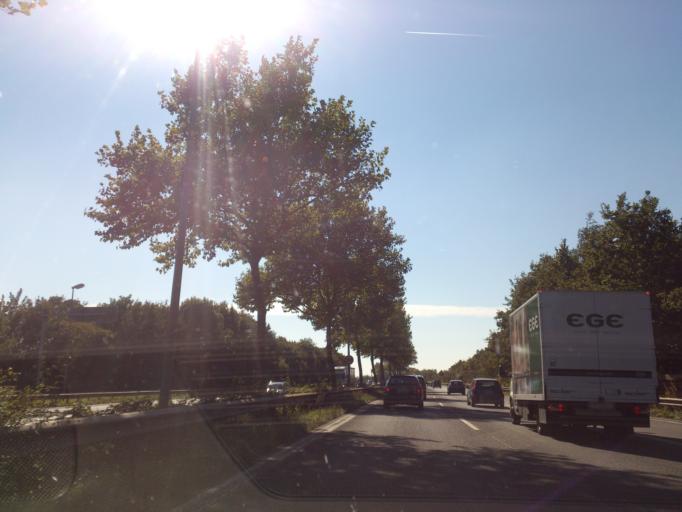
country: DE
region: North Rhine-Westphalia
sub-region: Regierungsbezirk Detmold
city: Bielefeld
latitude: 51.9973
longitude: 8.4973
